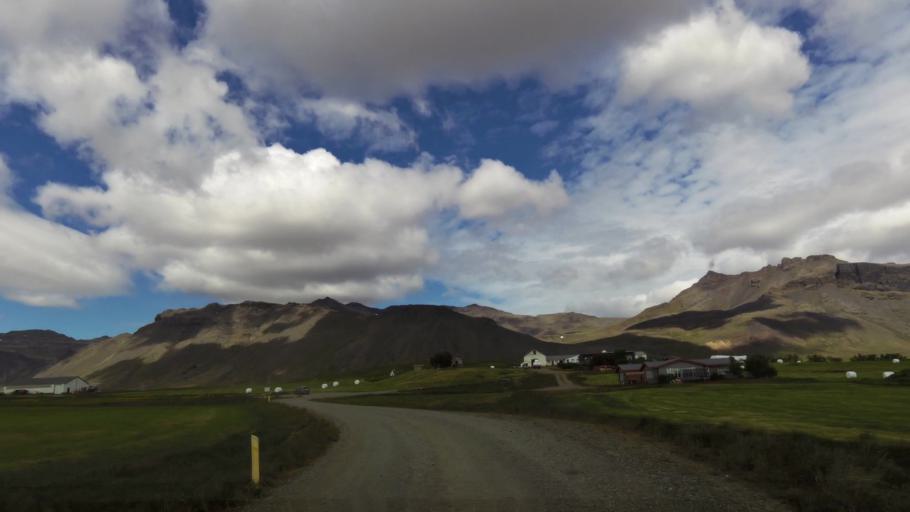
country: IS
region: West
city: Stykkisholmur
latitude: 64.8355
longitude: -22.9753
